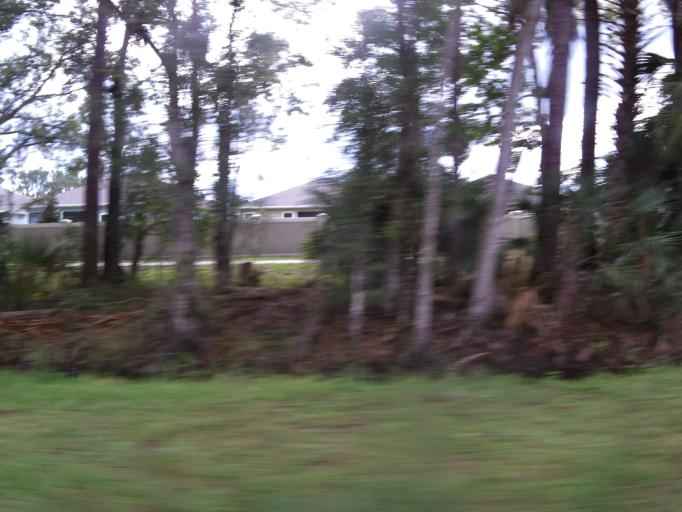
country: US
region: Florida
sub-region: Saint Johns County
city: Villano Beach
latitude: 29.9882
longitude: -81.4441
